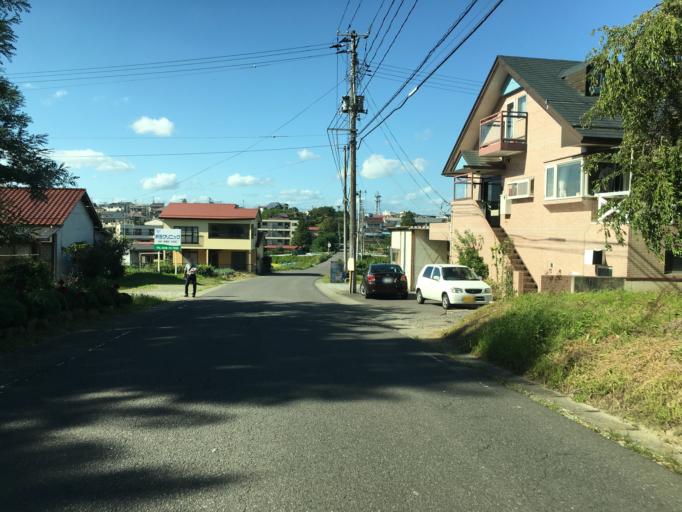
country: JP
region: Fukushima
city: Sukagawa
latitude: 37.2785
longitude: 140.3765
